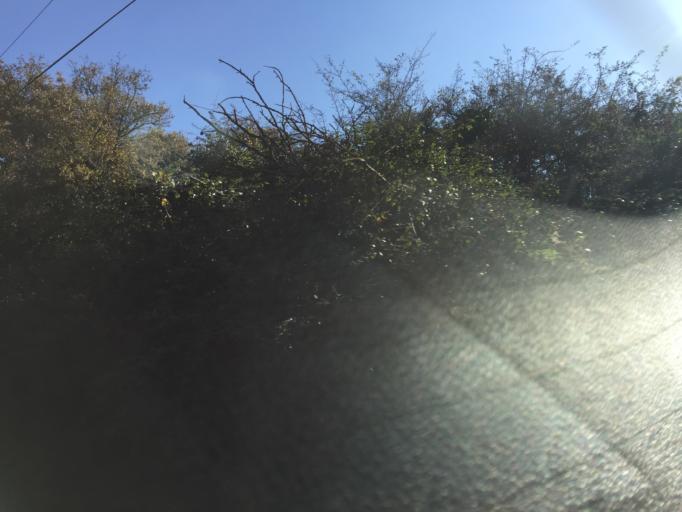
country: GB
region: England
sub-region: South Gloucestershire
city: Wickwar
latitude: 51.5840
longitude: -2.4071
